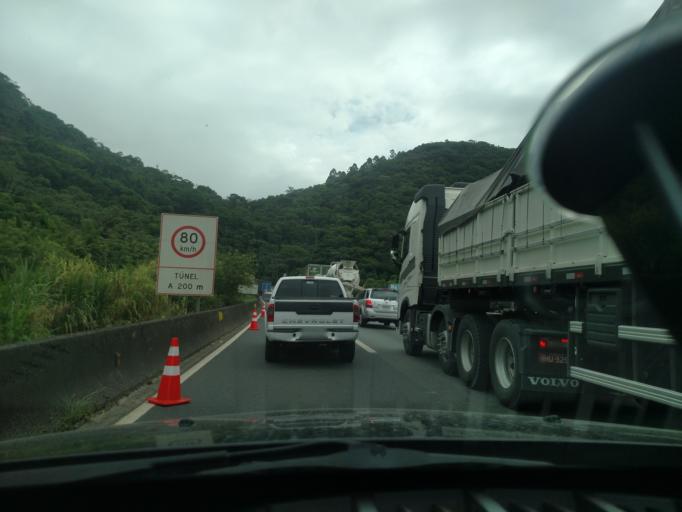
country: BR
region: Santa Catarina
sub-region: Itapema
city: Itapema
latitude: -27.0494
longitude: -48.5978
